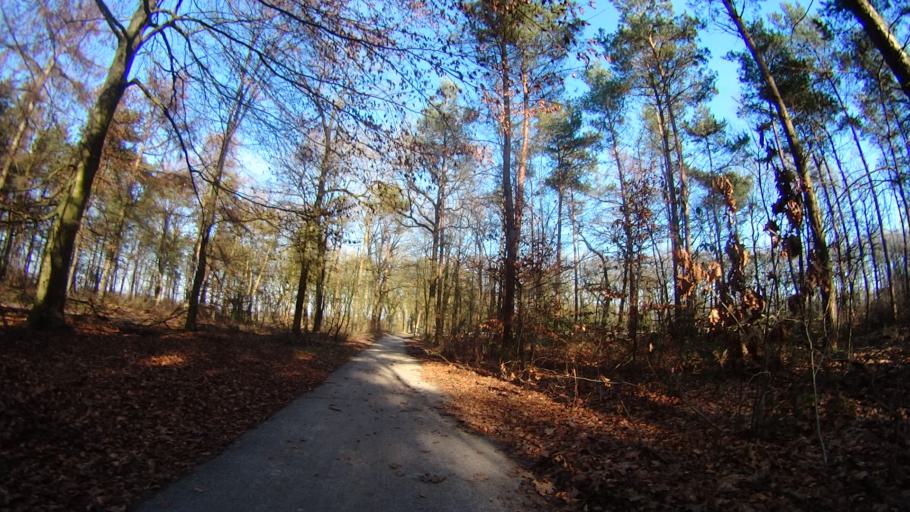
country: NL
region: Drenthe
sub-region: Gemeente Emmen
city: Emmen
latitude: 52.7783
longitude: 6.8623
